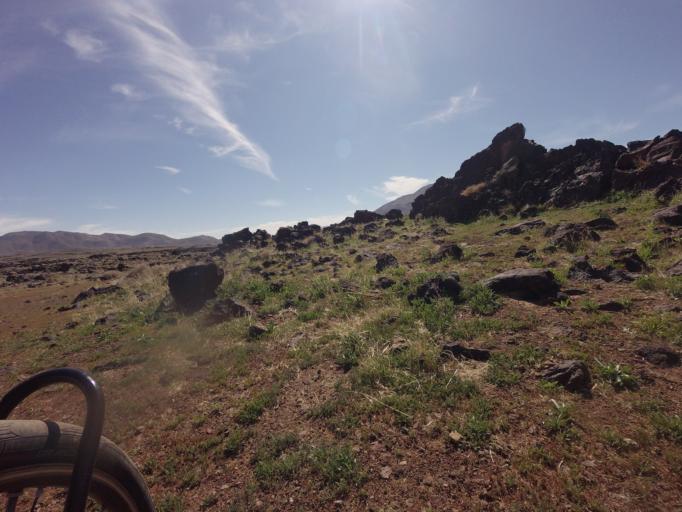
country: US
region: California
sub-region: Kern County
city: Inyokern
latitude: 35.9731
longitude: -117.9105
